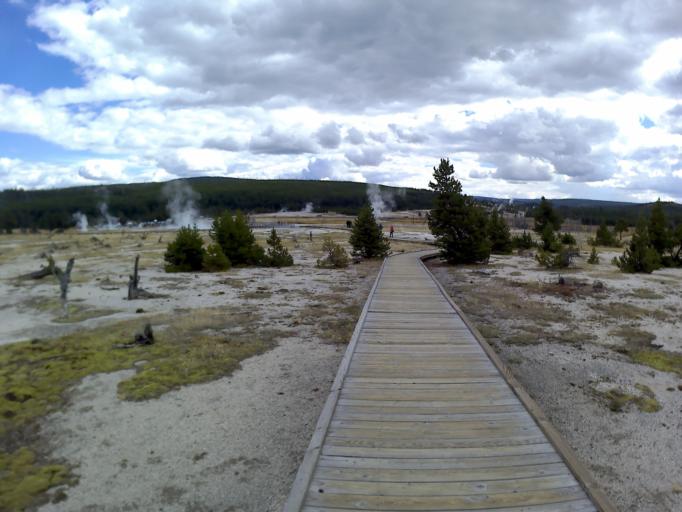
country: US
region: Montana
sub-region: Gallatin County
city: West Yellowstone
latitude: 44.4852
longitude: -110.8573
